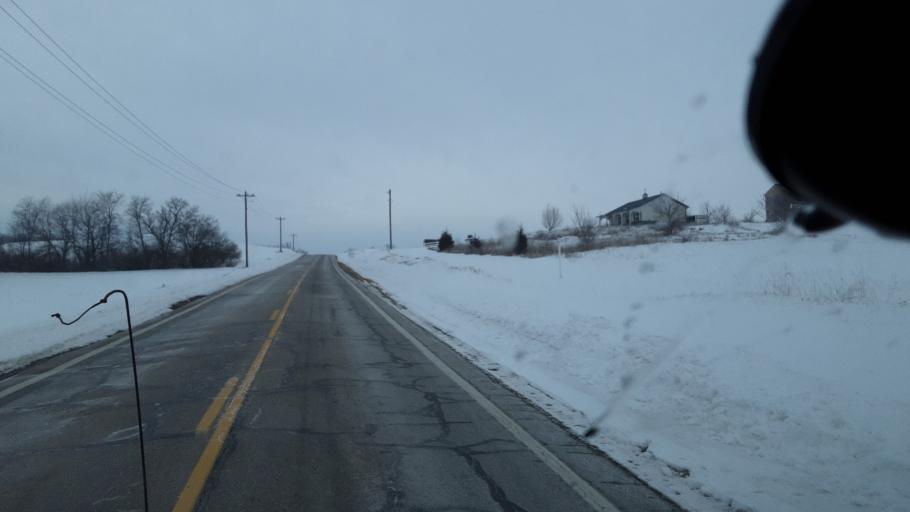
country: US
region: Ohio
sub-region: Champaign County
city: Mechanicsburg
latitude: 40.1004
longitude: -83.5561
